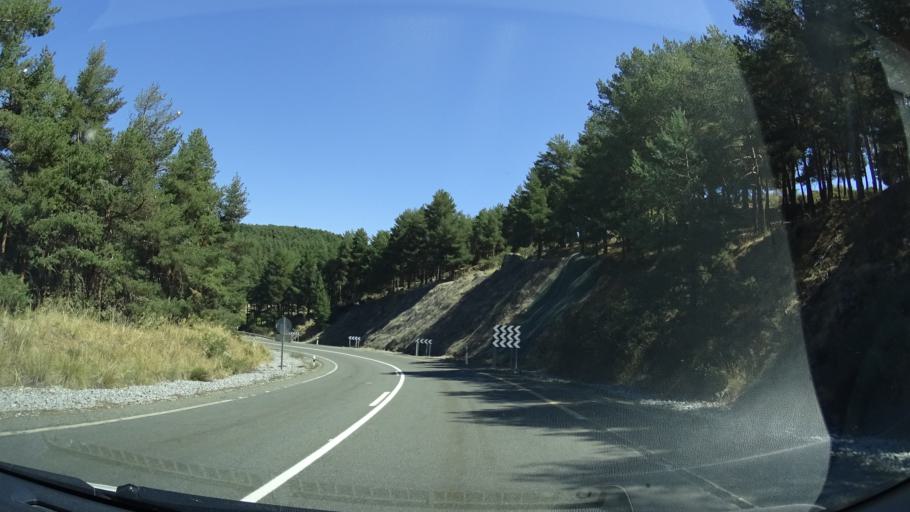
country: ES
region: Castille and Leon
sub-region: Provincia de Avila
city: Navalperal de Pinares
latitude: 40.6121
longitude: -4.4958
